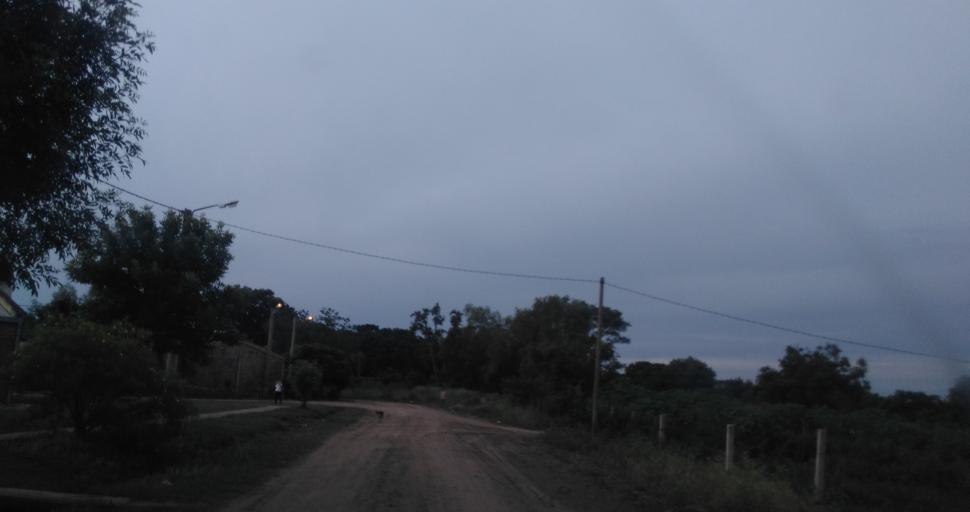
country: AR
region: Chaco
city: Fontana
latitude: -27.4110
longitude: -59.0252
